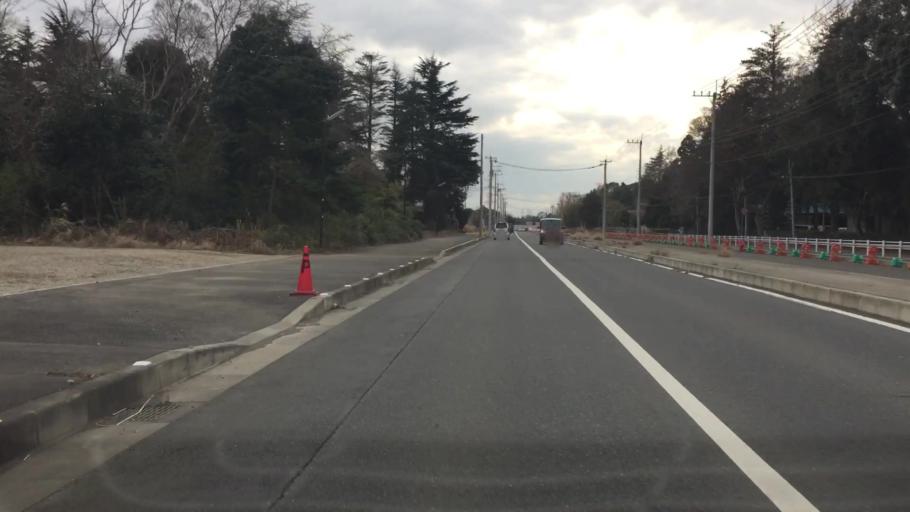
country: JP
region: Chiba
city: Shiroi
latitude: 35.7983
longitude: 140.0936
